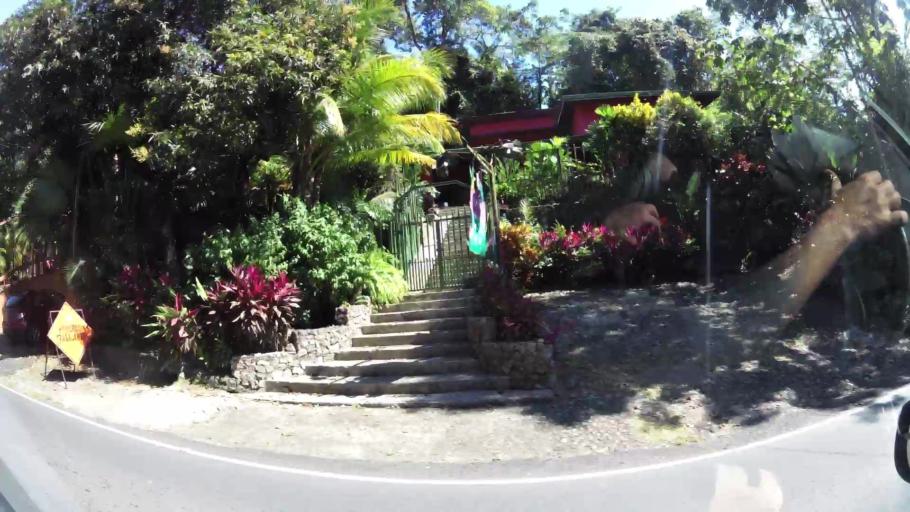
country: CR
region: Puntarenas
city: Quepos
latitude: 9.4178
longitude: -84.1580
